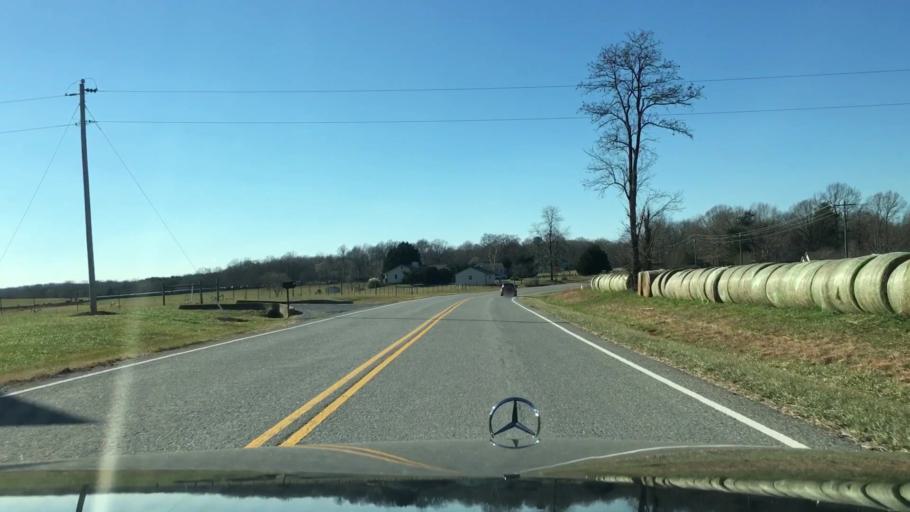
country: US
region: Virginia
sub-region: City of Bedford
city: Bedford
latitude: 37.2209
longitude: -79.4865
